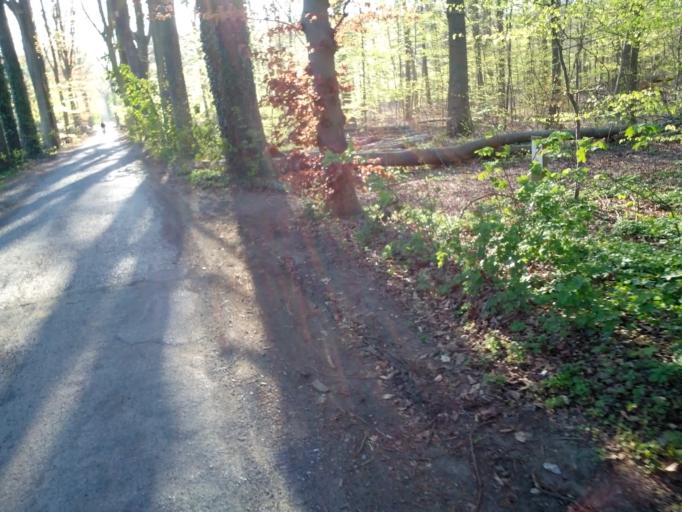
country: BE
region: Flanders
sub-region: Provincie Vlaams-Brabant
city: Oud-Heverlee
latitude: 50.8386
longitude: 4.7005
